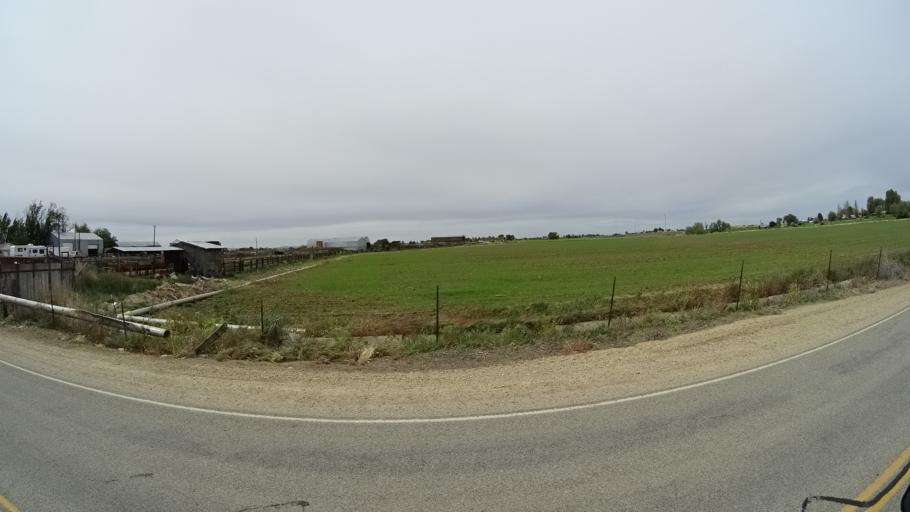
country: US
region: Idaho
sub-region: Ada County
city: Meridian
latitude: 43.5512
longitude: -116.3745
